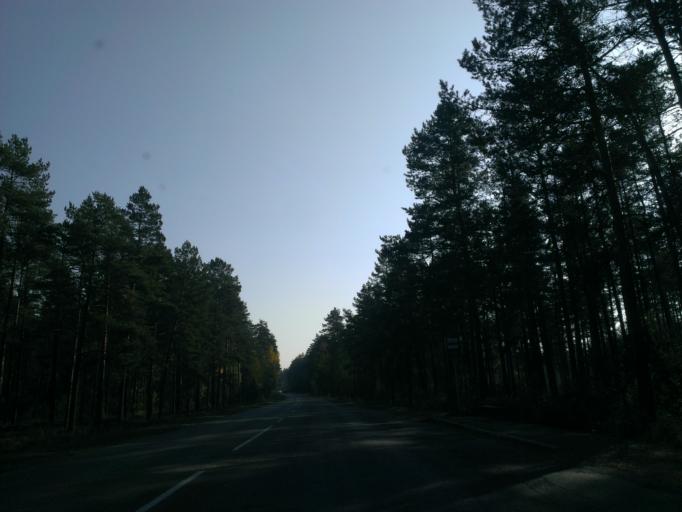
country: LV
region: Garkalne
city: Garkalne
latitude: 57.0368
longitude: 24.4176
